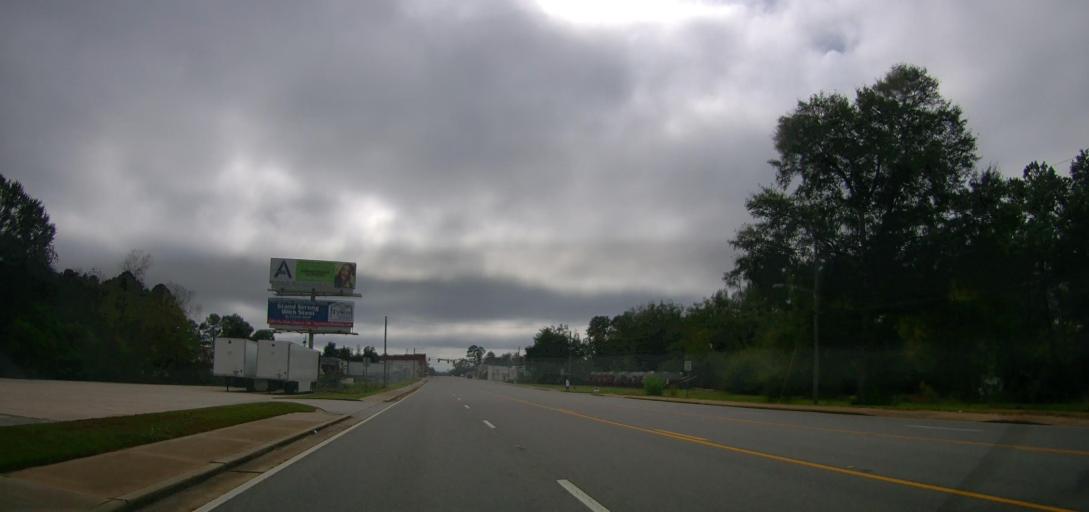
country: US
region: Georgia
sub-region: Colquitt County
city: Moultrie
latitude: 31.0134
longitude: -83.8659
